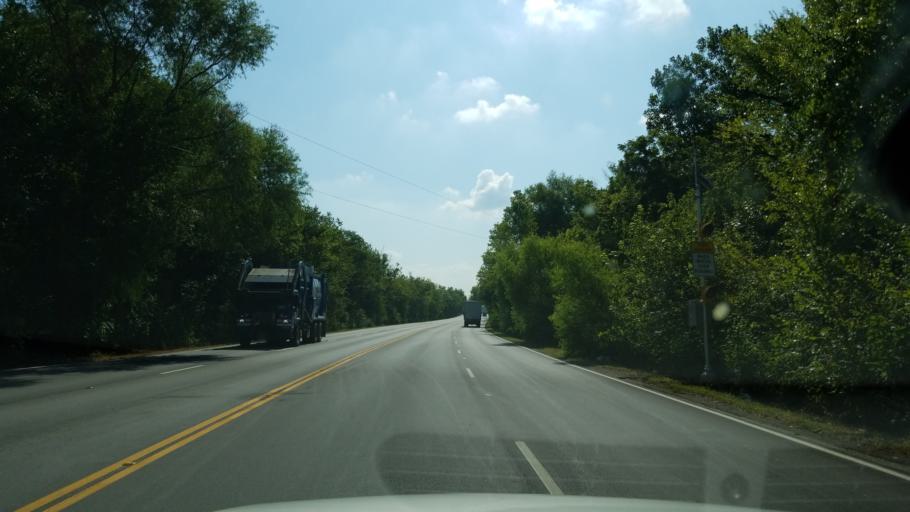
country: US
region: Texas
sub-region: Tarrant County
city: Hurst
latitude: 32.8022
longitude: -97.1562
